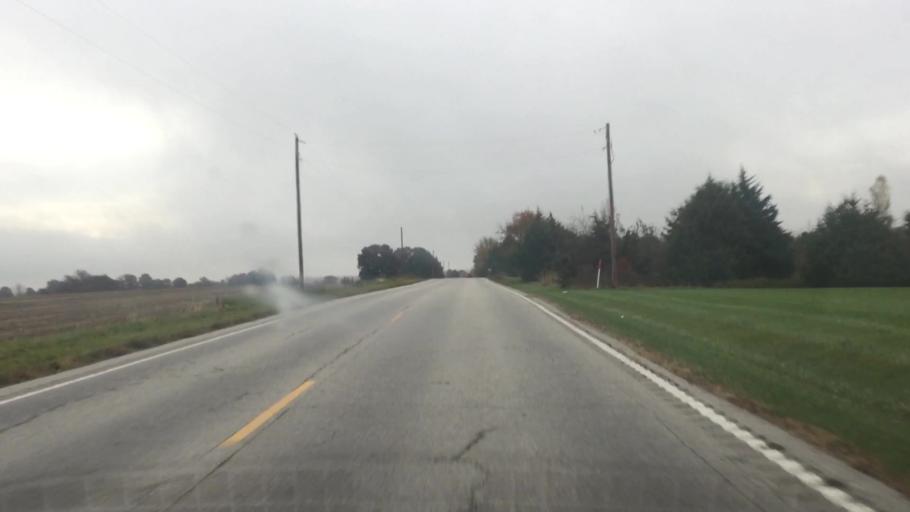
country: US
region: Missouri
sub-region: Boone County
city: Columbia
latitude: 38.9205
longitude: -92.1980
